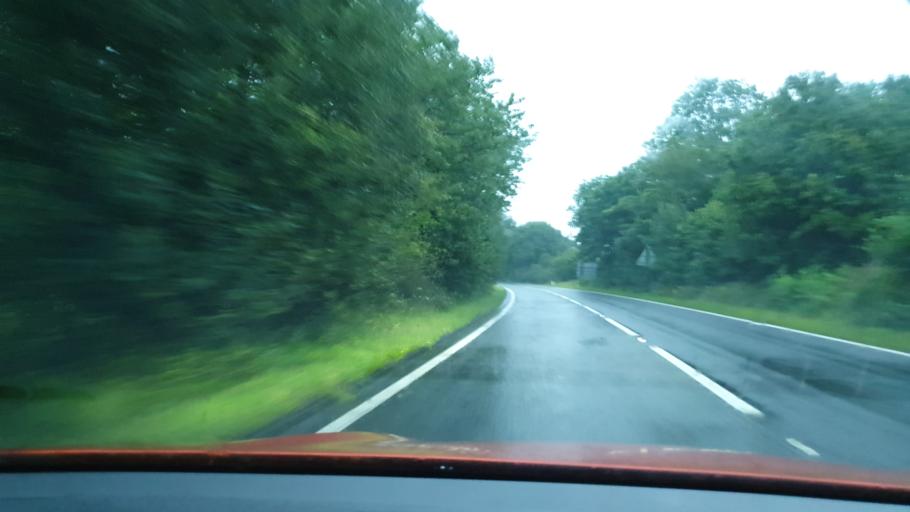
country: GB
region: England
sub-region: Cumbria
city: Grange-over-Sands
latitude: 54.2595
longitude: -2.9559
